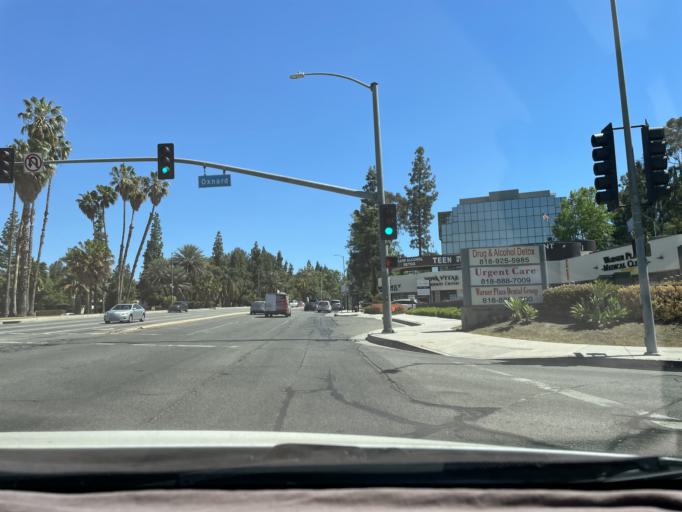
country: US
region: California
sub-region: Los Angeles County
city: Woodland Hills
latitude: 34.1793
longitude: -118.6056
